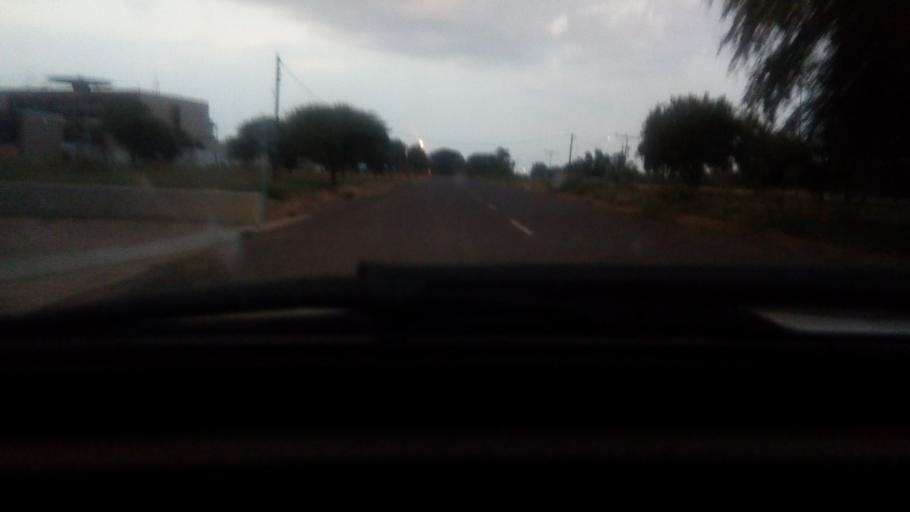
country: BW
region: Kweneng
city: Mmopone
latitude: -24.5886
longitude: 25.9167
